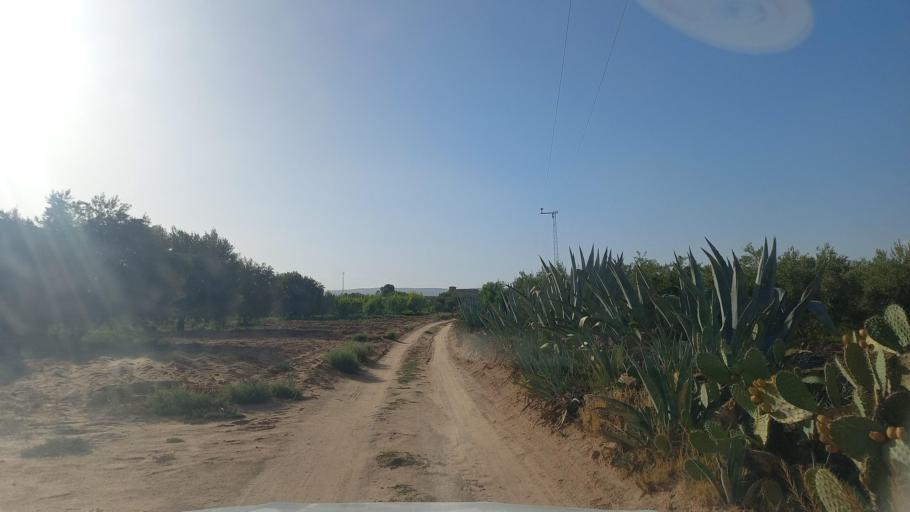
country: TN
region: Al Qasrayn
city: Kasserine
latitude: 35.2629
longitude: 9.0265
